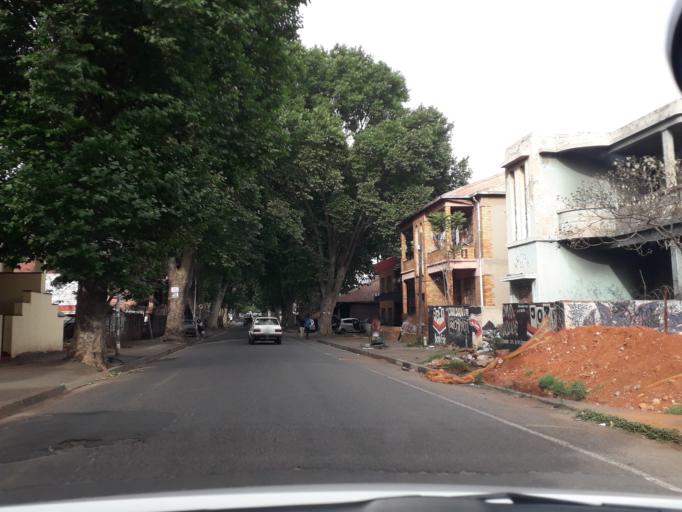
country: ZA
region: Gauteng
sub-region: City of Johannesburg Metropolitan Municipality
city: Johannesburg
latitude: -26.1915
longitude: 28.0630
